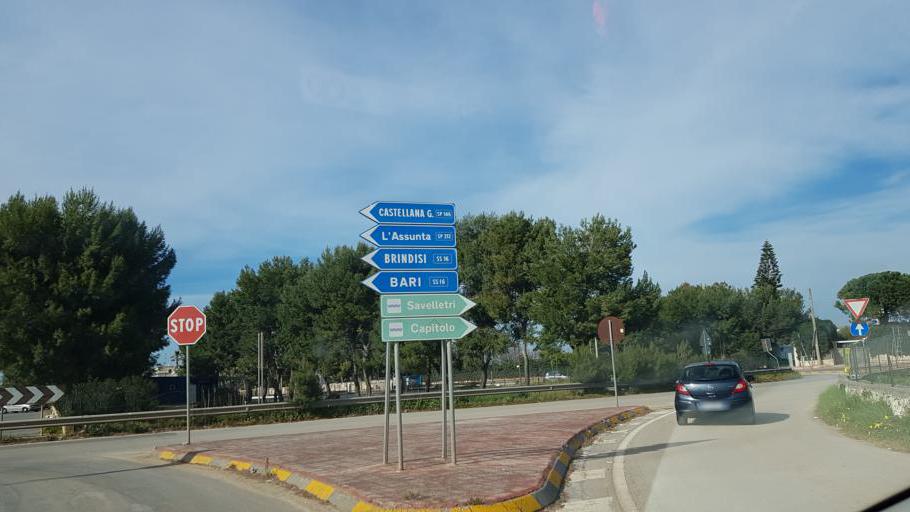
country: IT
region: Apulia
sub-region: Provincia di Brindisi
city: Fasano
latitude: 40.9042
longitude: 17.3500
